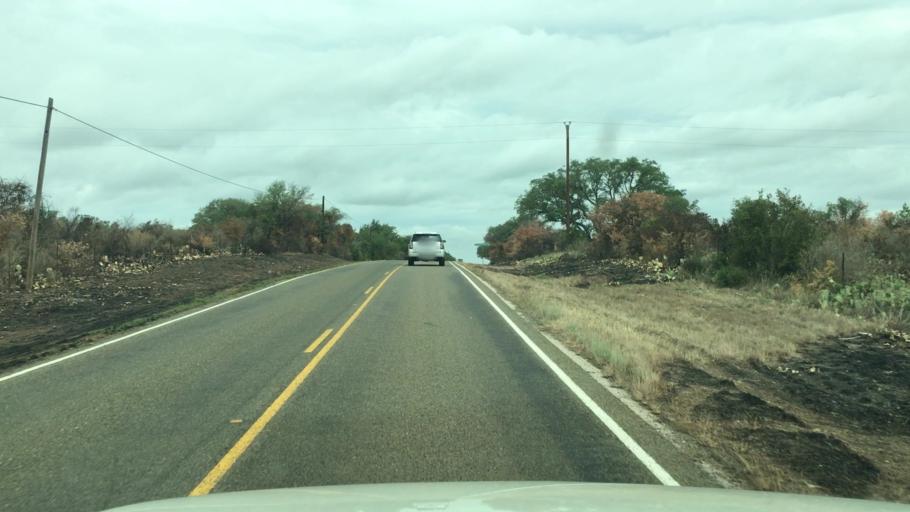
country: US
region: Texas
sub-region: Llano County
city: Horseshoe Bay
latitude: 30.4803
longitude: -98.4221
